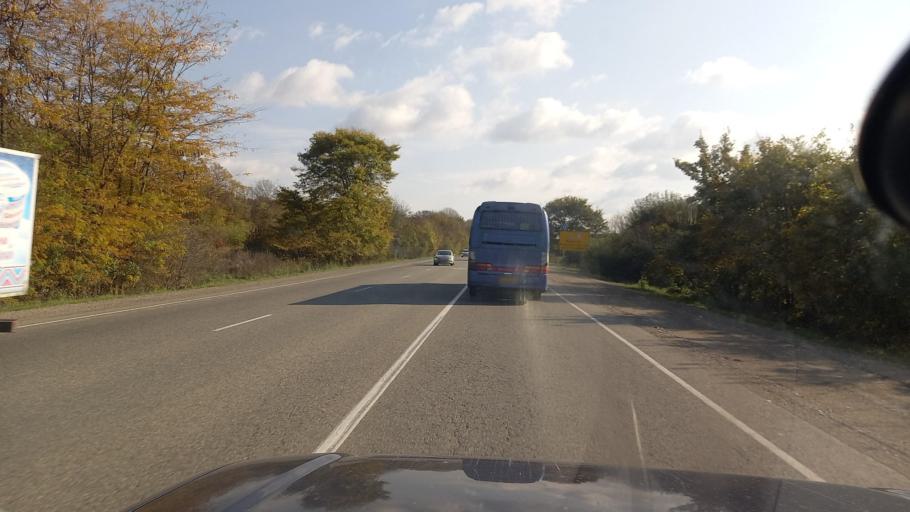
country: RU
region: Krasnodarskiy
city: Verkhnebakanskiy
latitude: 44.8737
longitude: 37.7621
